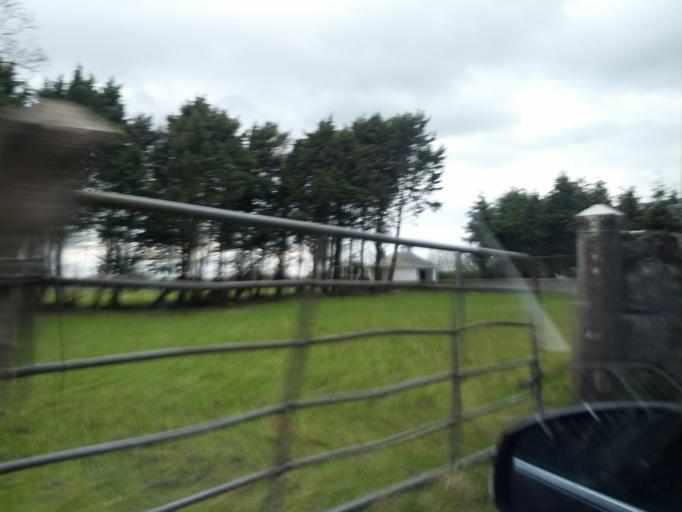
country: IE
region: Connaught
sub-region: County Galway
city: Athenry
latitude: 53.4153
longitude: -8.6354
